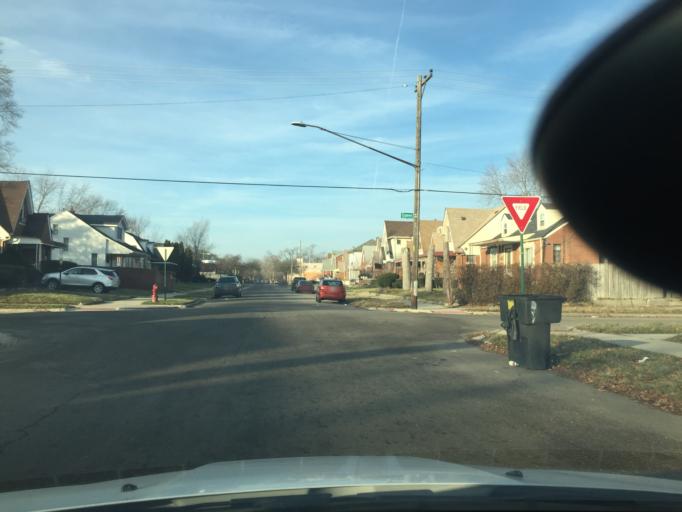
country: US
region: Michigan
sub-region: Macomb County
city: Eastpointe
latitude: 42.4444
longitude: -82.9687
